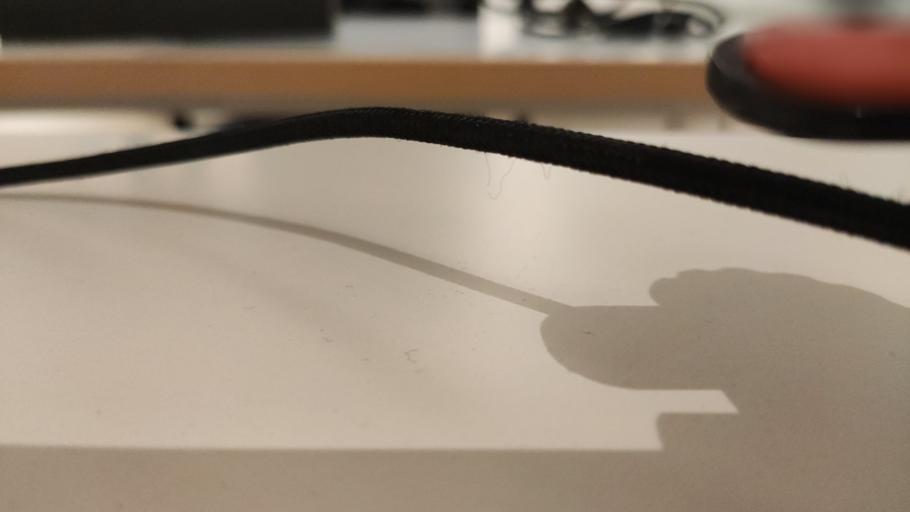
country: RU
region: Moskovskaya
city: Dorokhovo
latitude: 55.4158
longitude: 36.3667
